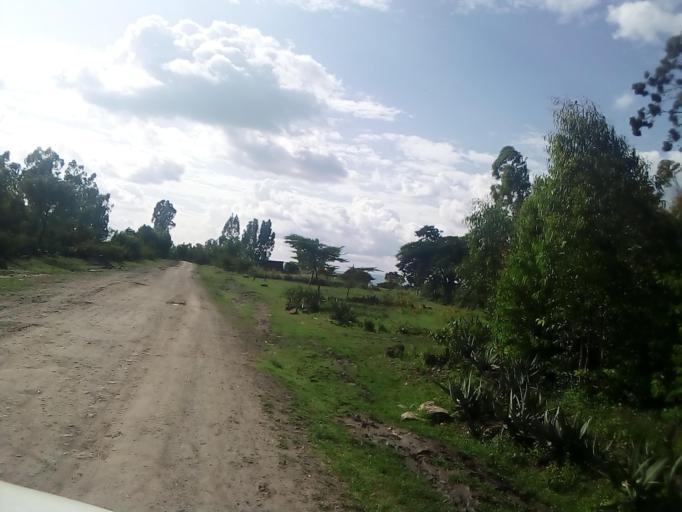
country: ET
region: Southern Nations, Nationalities, and People's Region
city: K'olito
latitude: 7.6405
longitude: 38.0577
